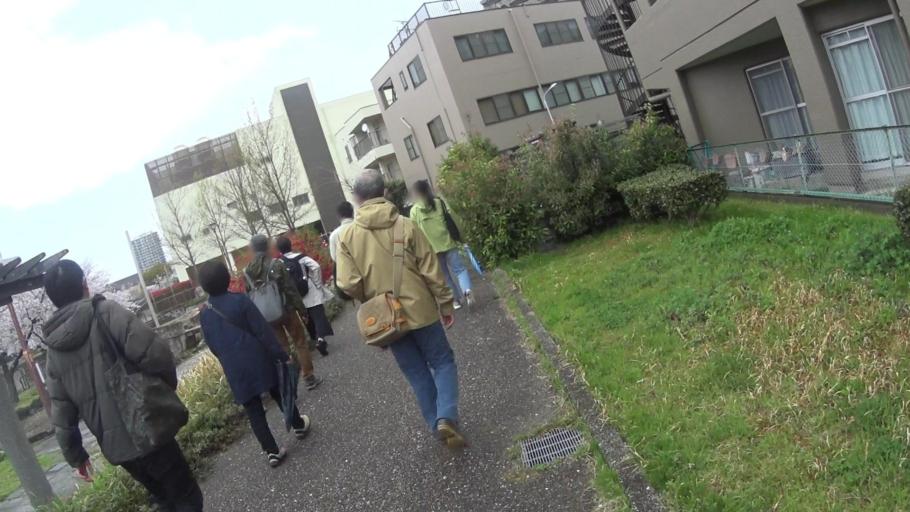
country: JP
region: Aichi
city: Nagoya-shi
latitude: 35.1223
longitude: 136.9029
